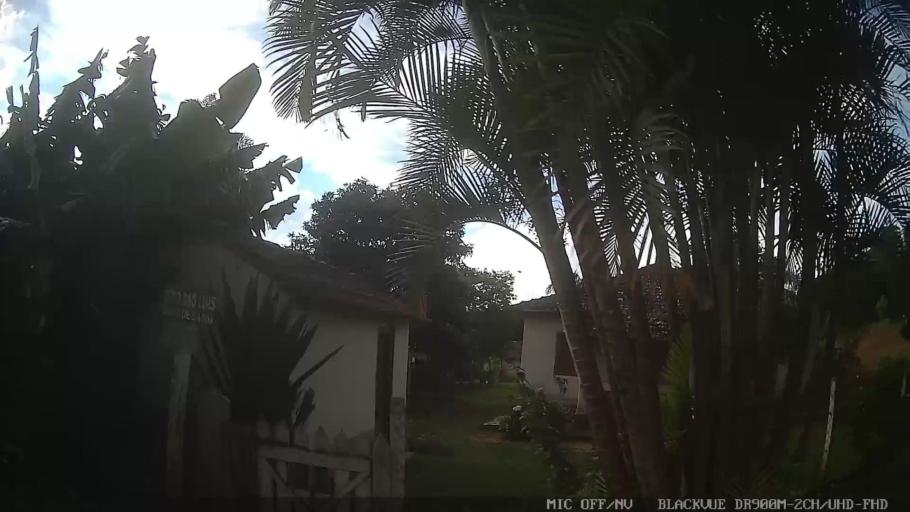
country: BR
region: Minas Gerais
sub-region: Extrema
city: Extrema
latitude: -22.8456
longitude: -46.2848
